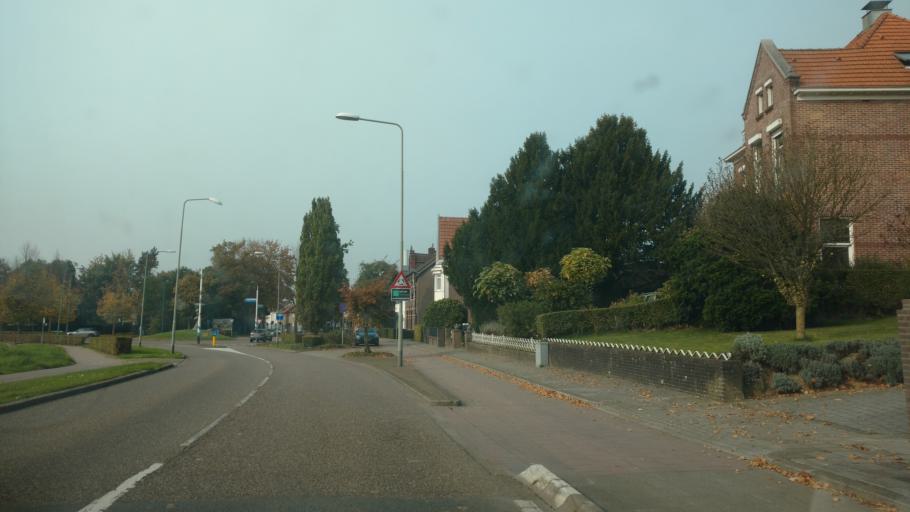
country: NL
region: Limburg
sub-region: Gemeente Meerssen
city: Meerssen
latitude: 50.8835
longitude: 5.7618
